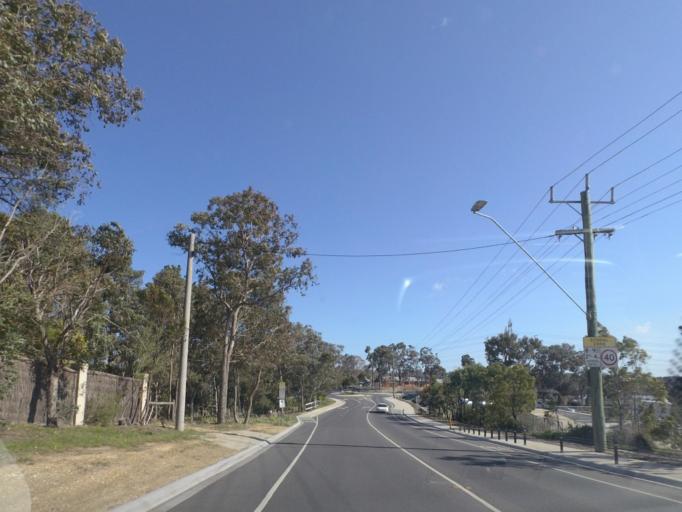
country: AU
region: Victoria
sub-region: Manningham
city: Park Orchards
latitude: -37.7733
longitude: 145.1962
